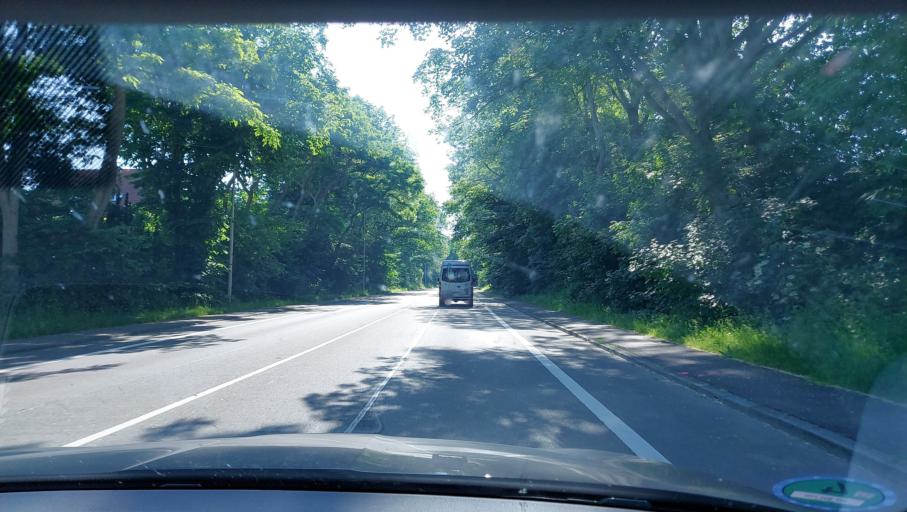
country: DE
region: North Rhine-Westphalia
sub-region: Regierungsbezirk Dusseldorf
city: Solingen
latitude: 51.1522
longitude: 7.0747
